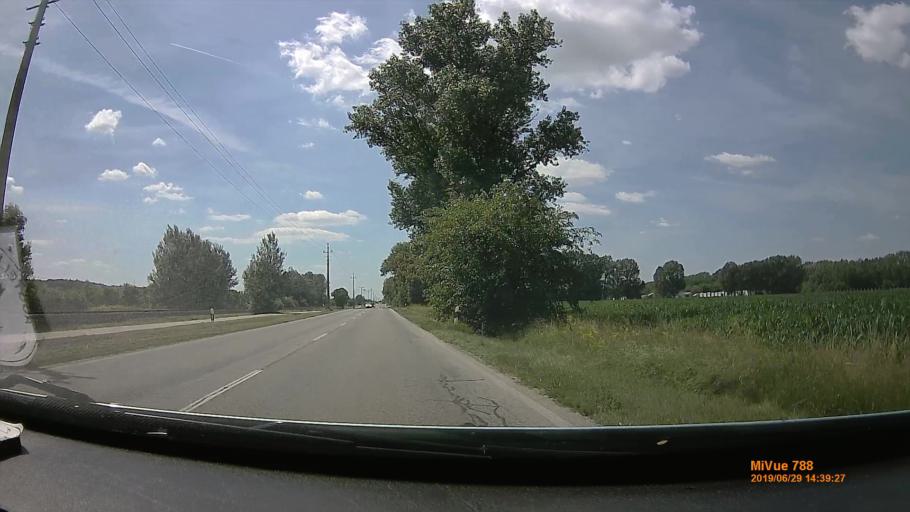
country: HU
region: Komarom-Esztergom
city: Tat
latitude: 47.7536
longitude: 18.6045
